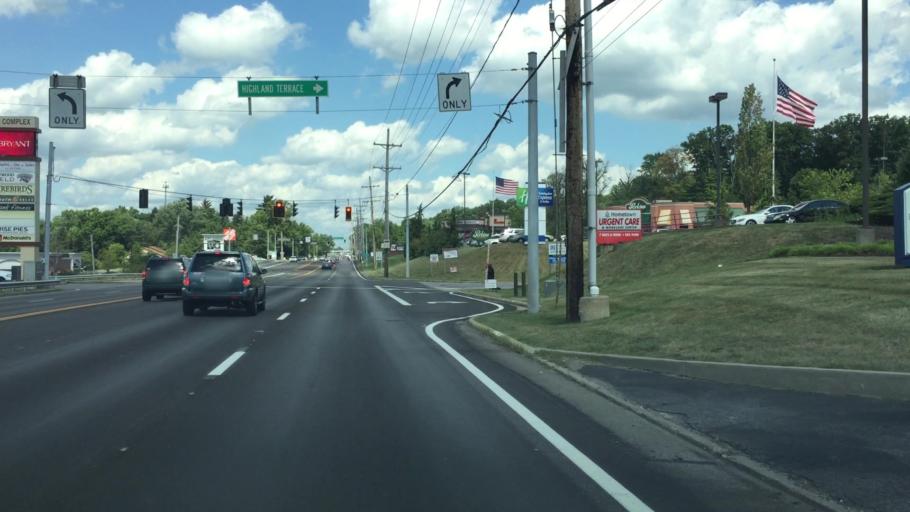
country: US
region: Ohio
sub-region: Trumbull County
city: Howland Center
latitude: 41.2154
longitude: -80.7403
